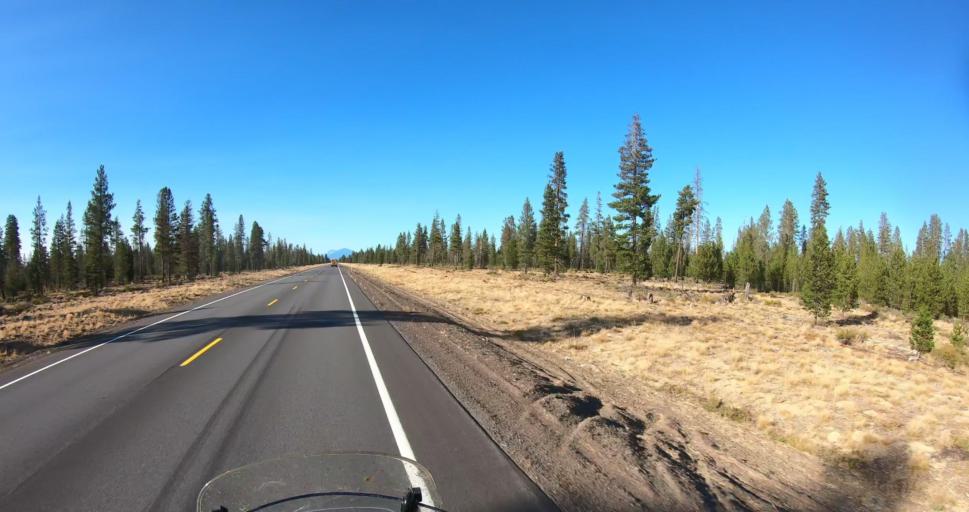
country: US
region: Oregon
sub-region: Deschutes County
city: La Pine
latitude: 43.5836
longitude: -121.4888
